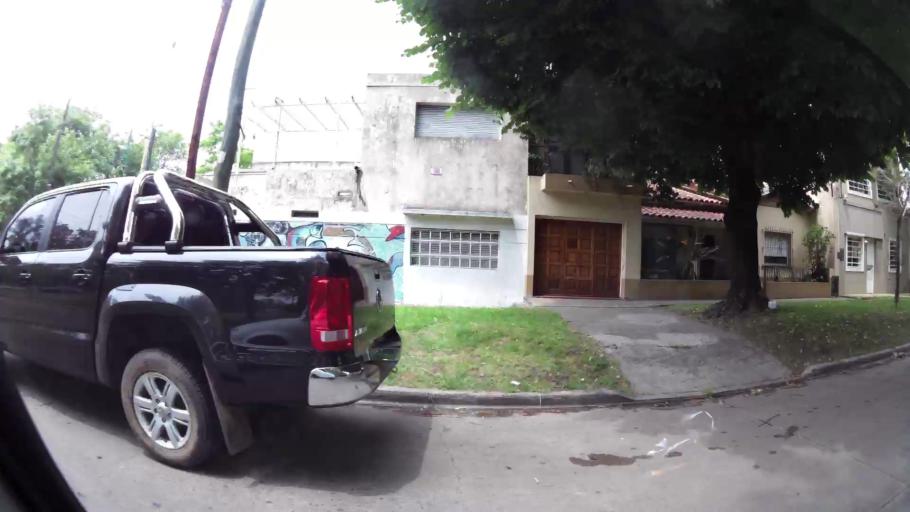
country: AR
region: Buenos Aires
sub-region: Partido de La Plata
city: La Plata
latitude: -34.9348
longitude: -57.9690
